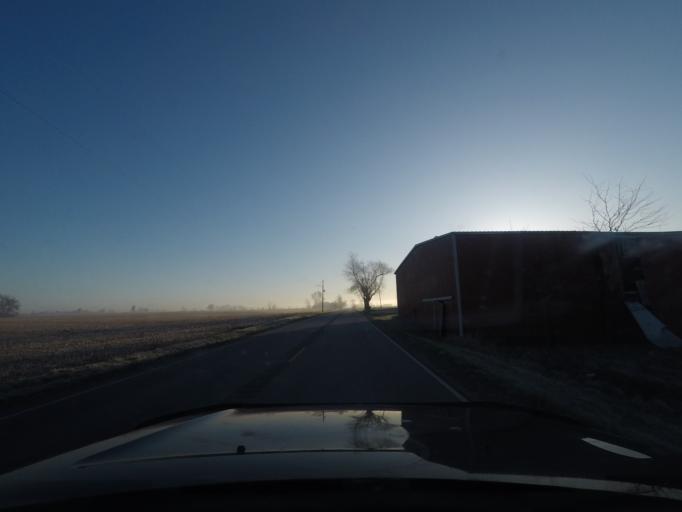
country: US
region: Indiana
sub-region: Elkhart County
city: Wakarusa
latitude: 41.5114
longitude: -85.9912
